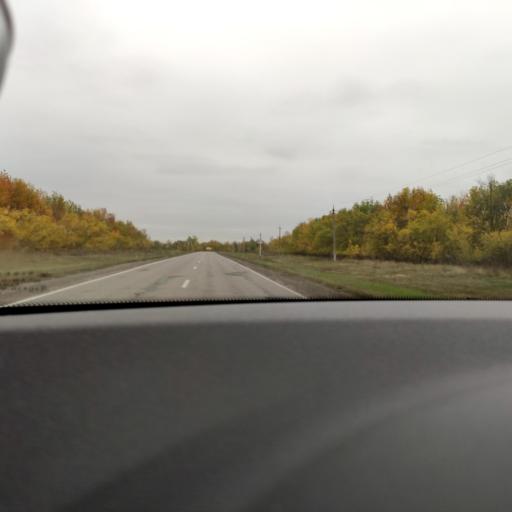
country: RU
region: Samara
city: Krasnyy Yar
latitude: 53.5108
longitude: 50.3398
